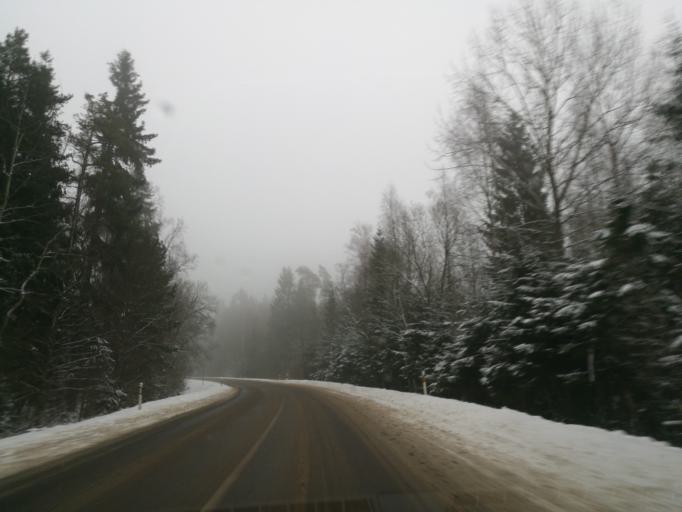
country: LT
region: Utenos apskritis
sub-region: Anyksciai
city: Anyksciai
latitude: 55.4700
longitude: 25.0712
